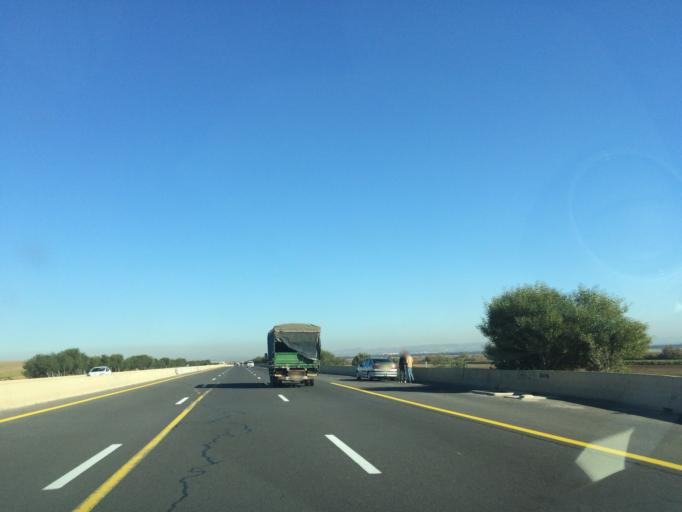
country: DZ
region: Relizane
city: Relizane
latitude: 35.8038
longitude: 0.6085
